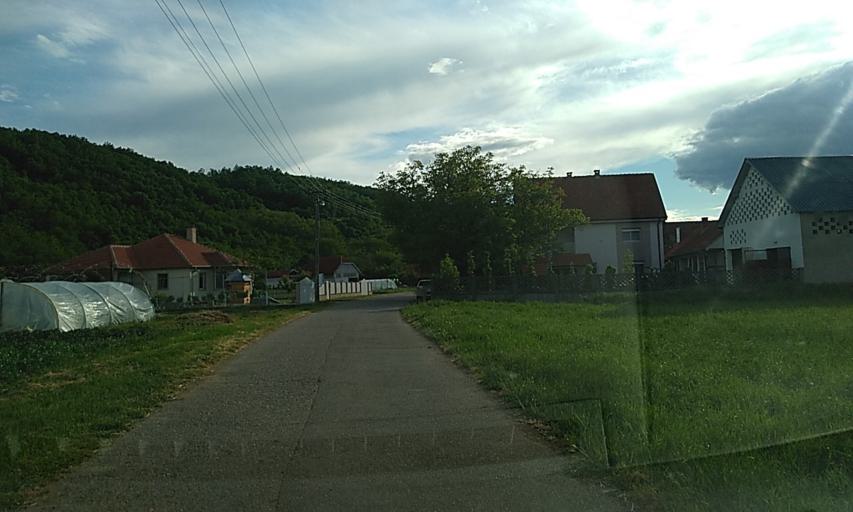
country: RS
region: Central Serbia
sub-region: Nisavski Okrug
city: Aleksinac
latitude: 43.4369
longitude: 21.7357
